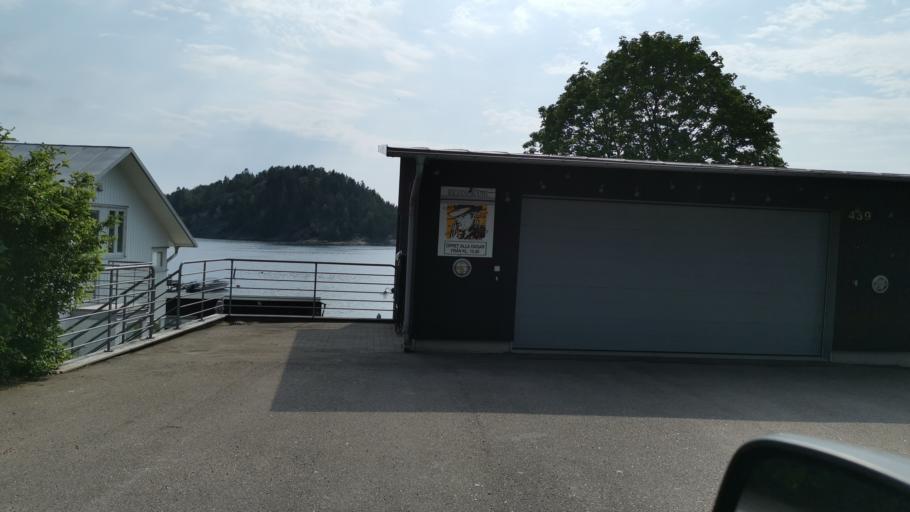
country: SE
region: Vaestra Goetaland
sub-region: Orust
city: Henan
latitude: 58.3100
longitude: 11.6950
